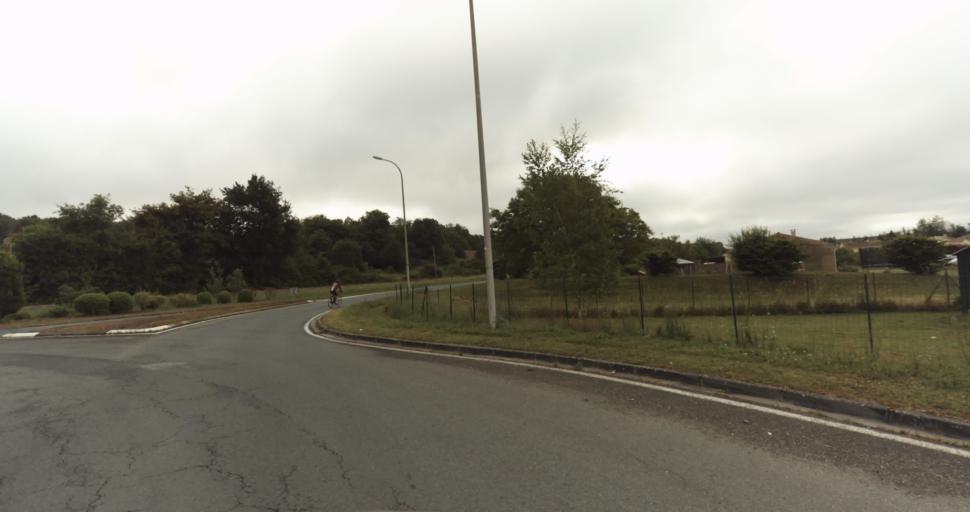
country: FR
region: Aquitaine
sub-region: Departement de la Dordogne
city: Mouleydier
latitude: 44.8517
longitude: 0.6148
